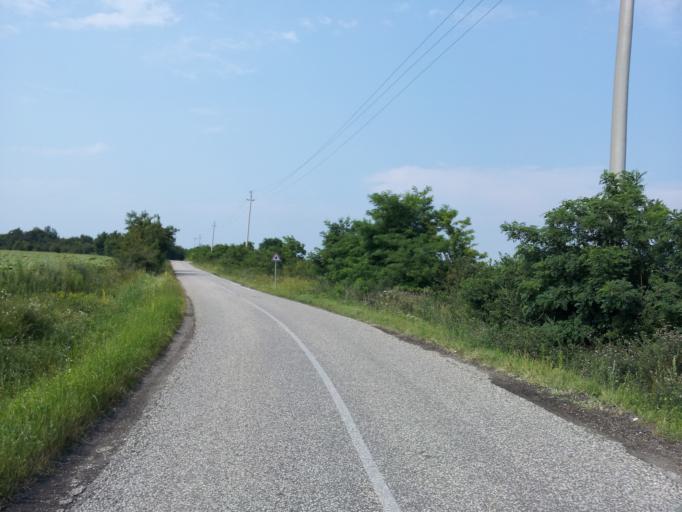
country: HU
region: Pest
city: Szigetujfalu
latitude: 47.2178
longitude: 18.9216
